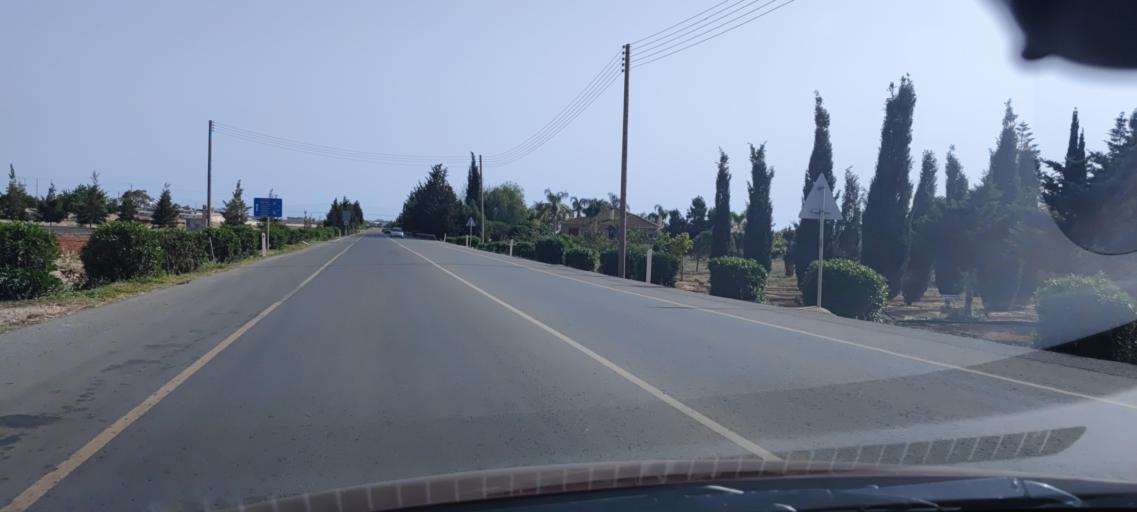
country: CY
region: Ammochostos
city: Frenaros
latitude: 35.0136
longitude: 33.9396
